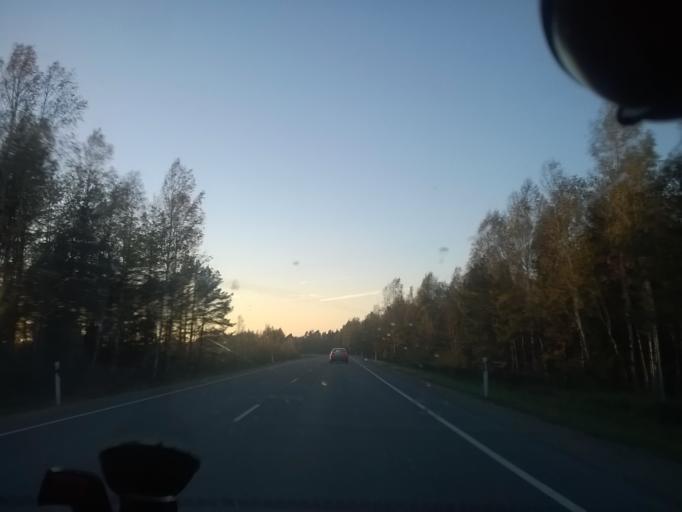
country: EE
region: Harju
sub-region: Nissi vald
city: Turba
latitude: 58.9938
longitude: 24.0500
